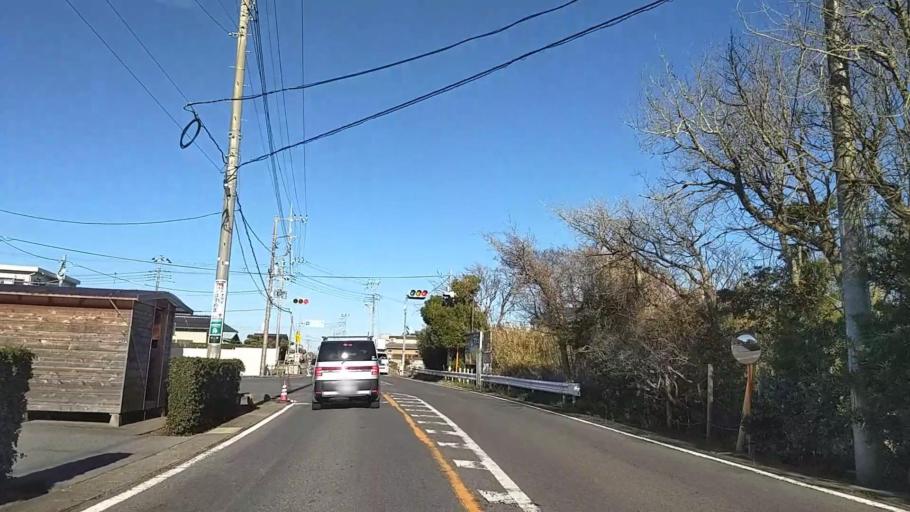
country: JP
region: Chiba
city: Naruto
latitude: 35.5777
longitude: 140.4890
